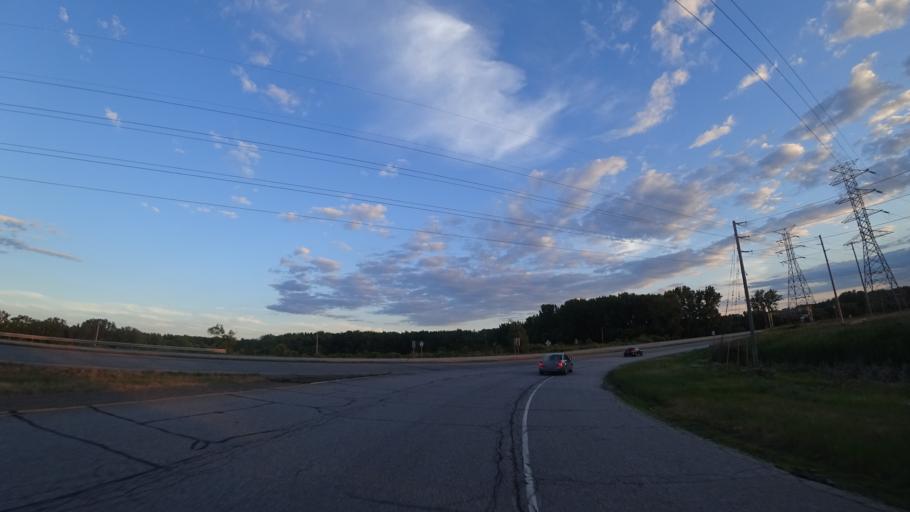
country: US
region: Indiana
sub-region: Porter County
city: Burns Harbor
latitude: 41.6177
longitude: -87.1573
